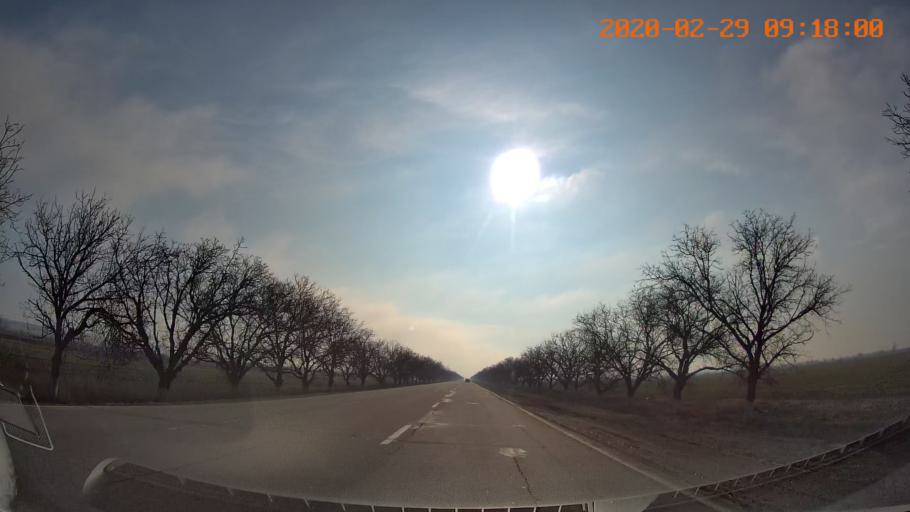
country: MD
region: Telenesti
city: Pervomaisc
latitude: 46.7776
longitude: 29.9148
